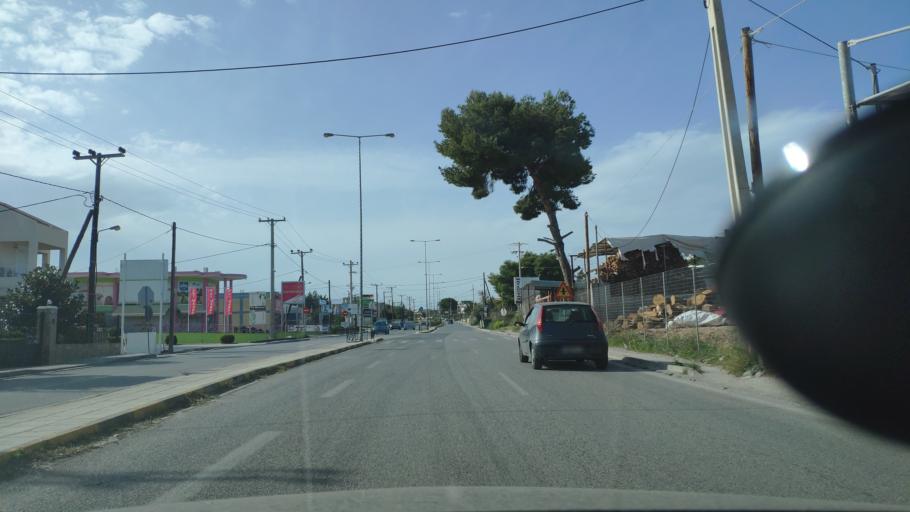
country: GR
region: Attica
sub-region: Nomarchia Anatolikis Attikis
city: Limin Mesoyaias
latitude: 37.8918
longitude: 23.9941
